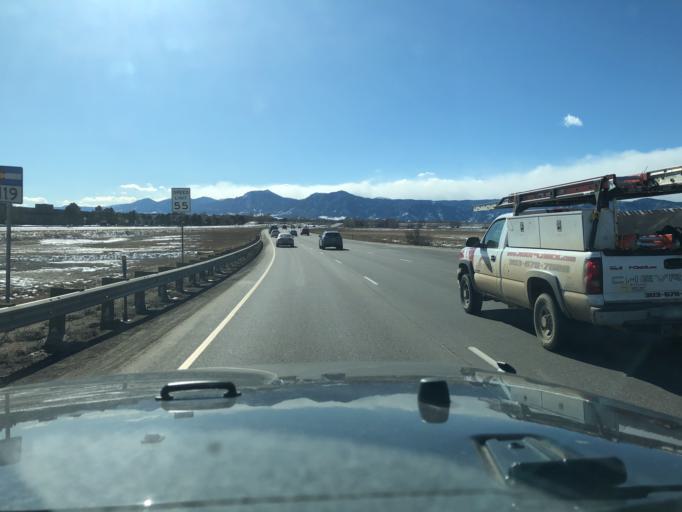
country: US
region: Colorado
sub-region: Boulder County
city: Gunbarrel
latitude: 40.0745
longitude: -105.2076
